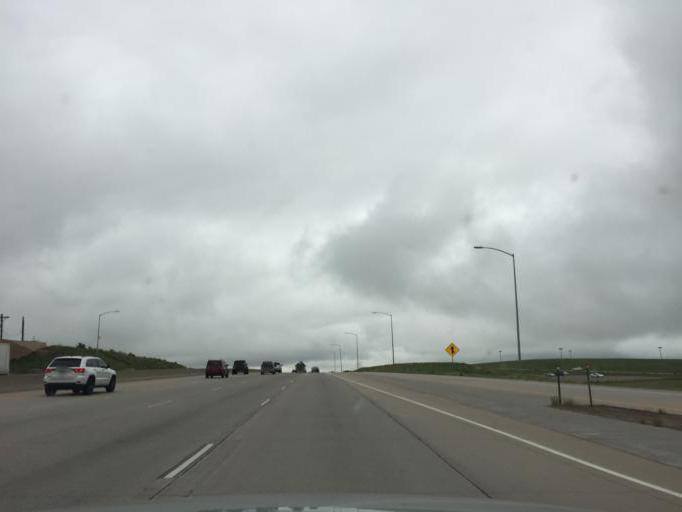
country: US
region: Colorado
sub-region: Park County
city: Castle Pines North
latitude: 39.4746
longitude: -104.8723
